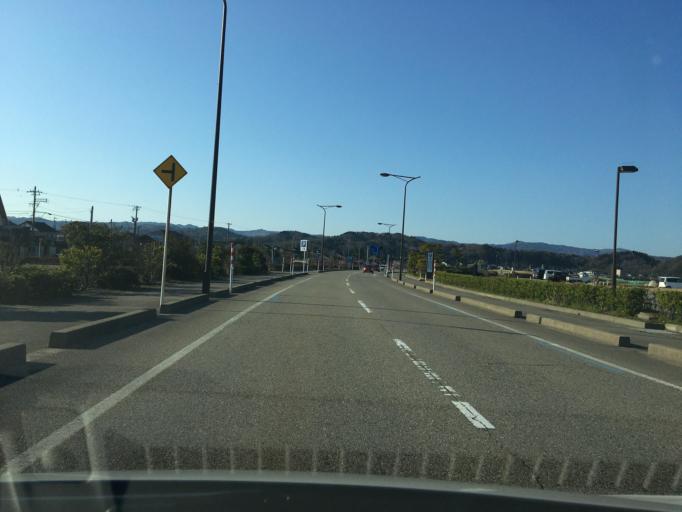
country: JP
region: Toyama
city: Himi
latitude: 36.8677
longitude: 136.9852
